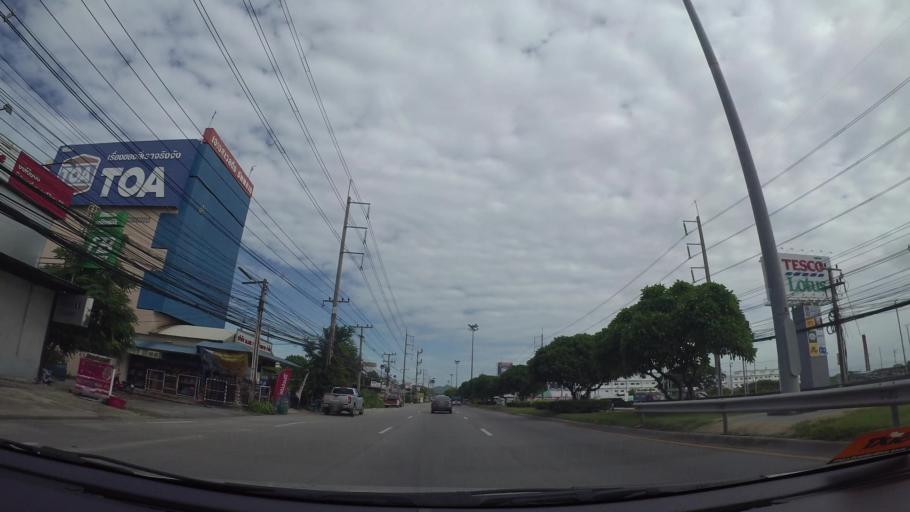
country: TH
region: Rayong
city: Rayong
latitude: 12.7153
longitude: 101.1649
